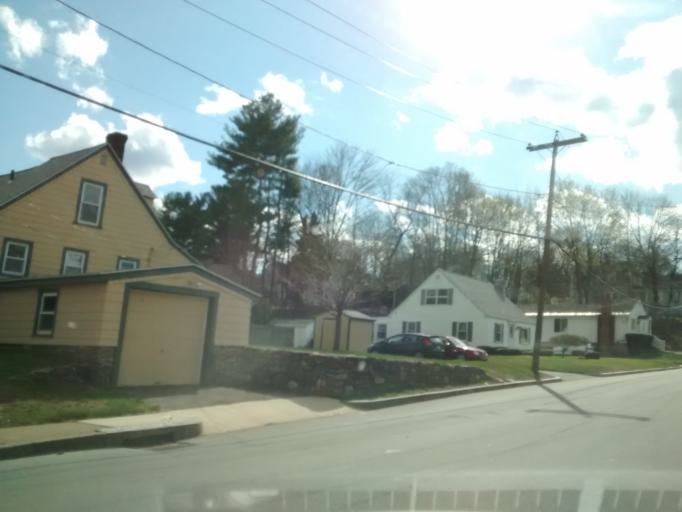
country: US
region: Massachusetts
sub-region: Worcester County
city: Worcester
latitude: 42.3044
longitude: -71.8181
